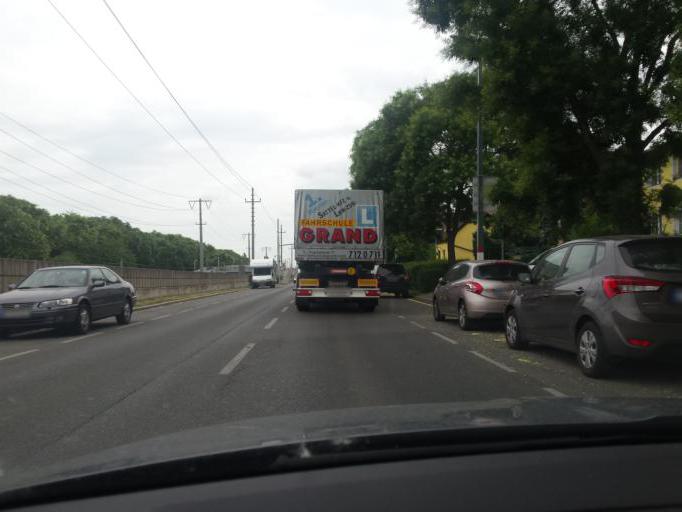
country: AT
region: Lower Austria
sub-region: Politischer Bezirk Wien-Umgebung
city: Leopoldsdorf
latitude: 48.1660
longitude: 16.4143
